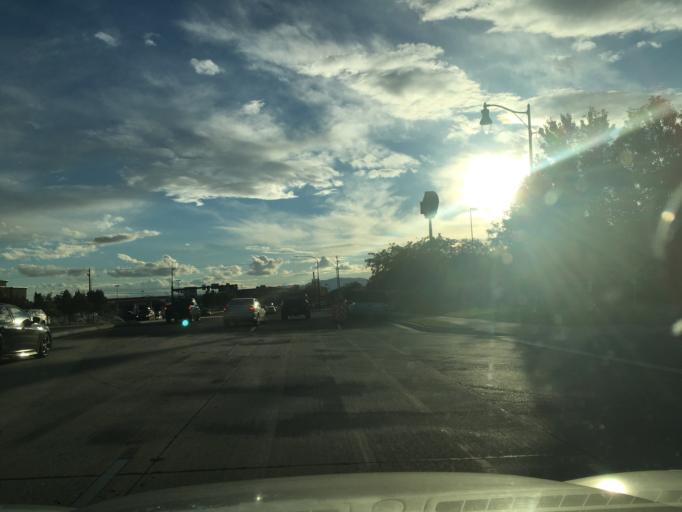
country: US
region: Utah
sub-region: Davis County
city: Layton
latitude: 41.0737
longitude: -111.9774
